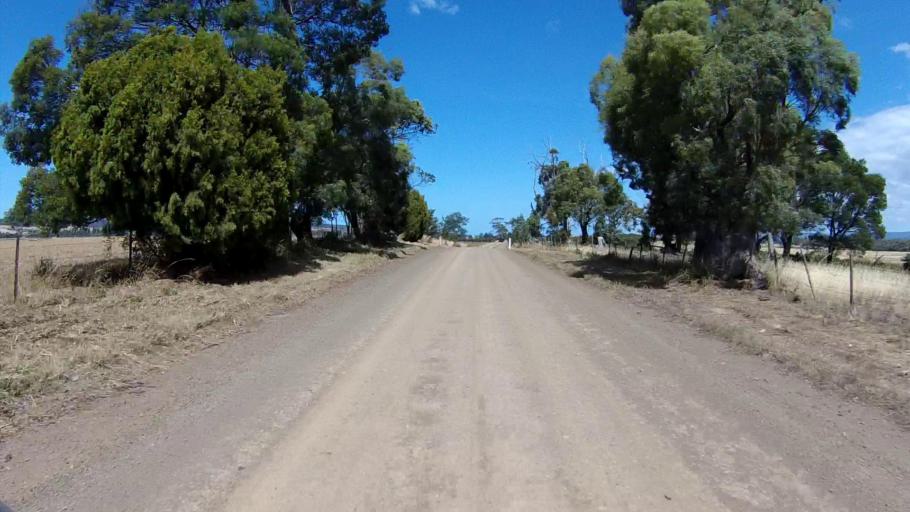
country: AU
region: Tasmania
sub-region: Break O'Day
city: St Helens
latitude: -41.9920
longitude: 148.0670
